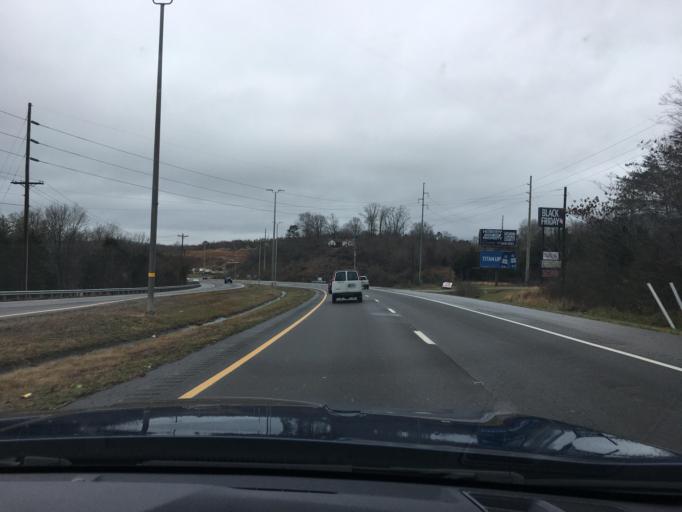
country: US
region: Tennessee
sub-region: McMinn County
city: Athens
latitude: 35.4552
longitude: -84.6284
